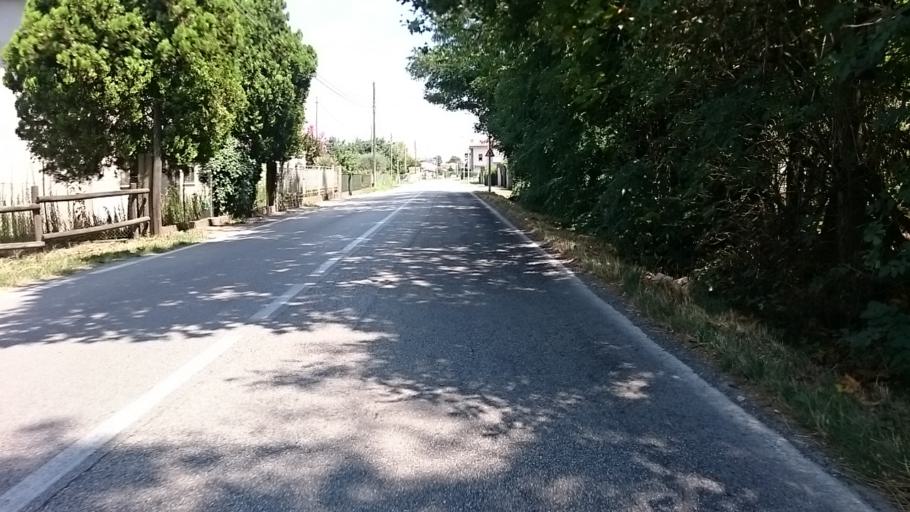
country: IT
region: Veneto
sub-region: Provincia di Vicenza
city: Rosa
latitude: 45.6930
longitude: 11.7409
